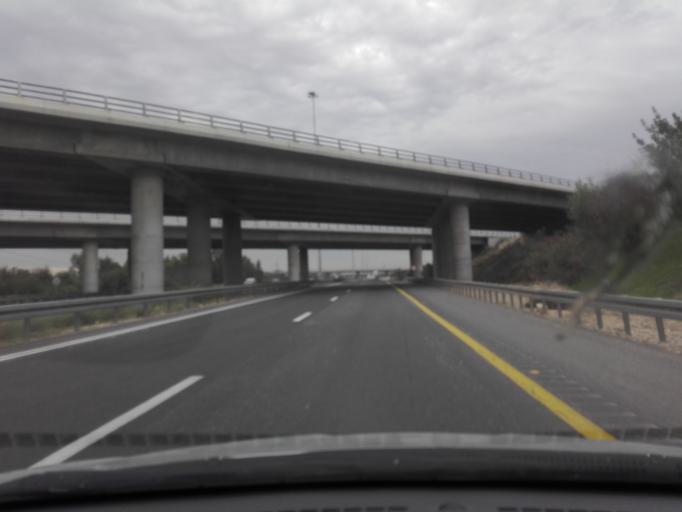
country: IL
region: Central District
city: Lod
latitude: 31.9112
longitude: 34.8976
